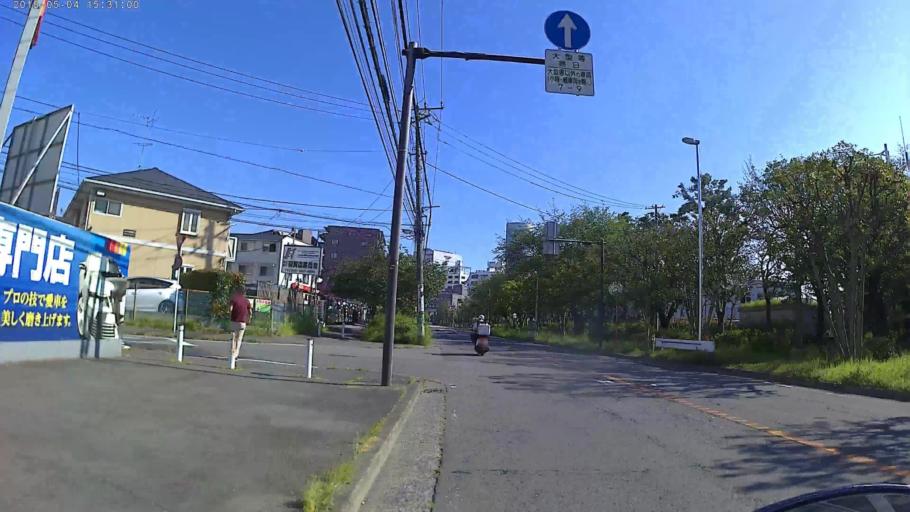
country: JP
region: Kanagawa
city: Yokohama
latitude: 35.5171
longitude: 139.6207
